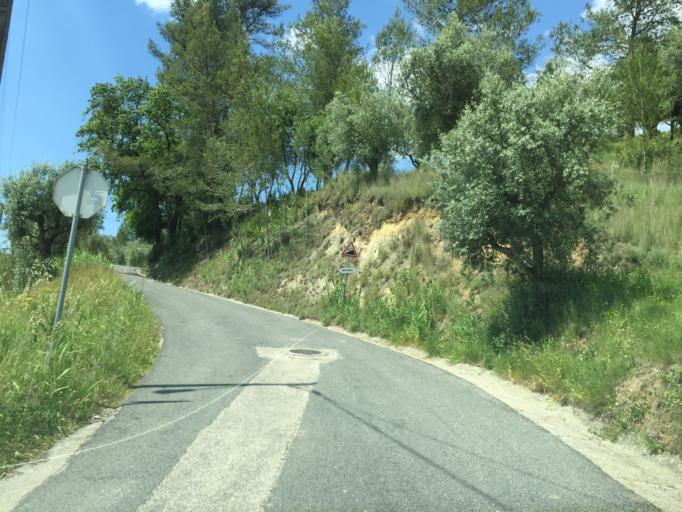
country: PT
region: Santarem
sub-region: Ourem
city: Ourem
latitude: 39.6678
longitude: -8.5742
